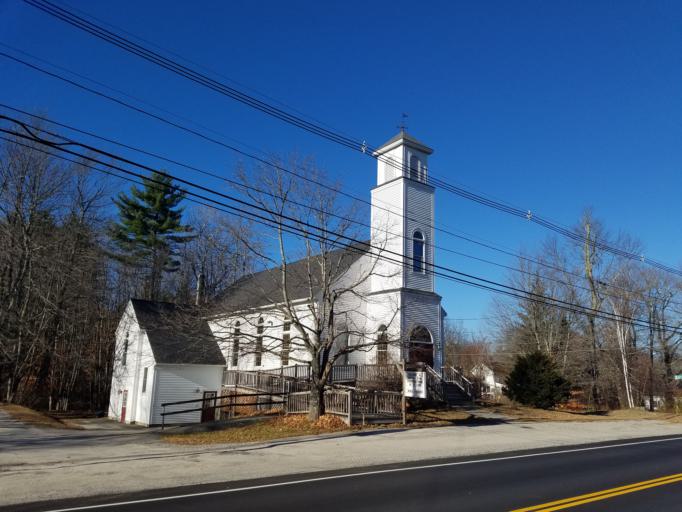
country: US
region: Maine
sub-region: York County
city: Buxton
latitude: 43.7359
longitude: -70.5506
